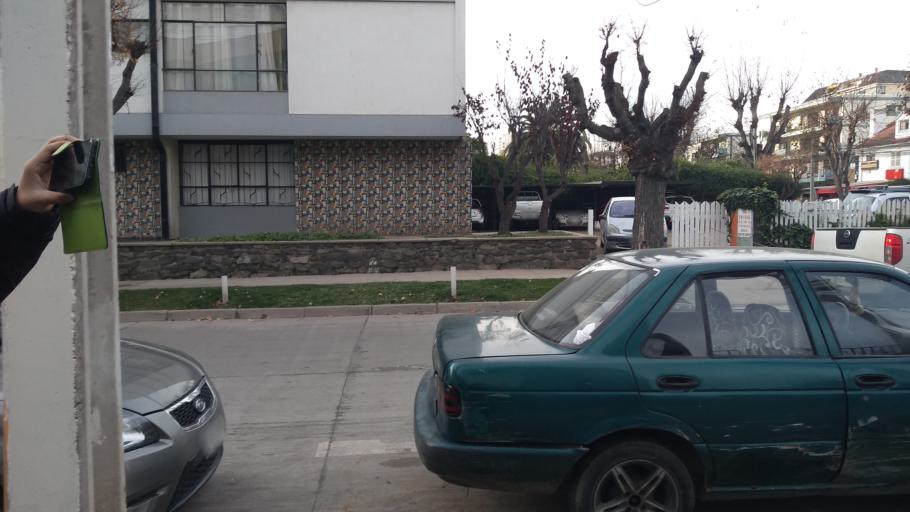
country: CL
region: Valparaiso
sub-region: Provincia de Valparaiso
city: Vina del Mar
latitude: -33.0208
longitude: -71.5566
